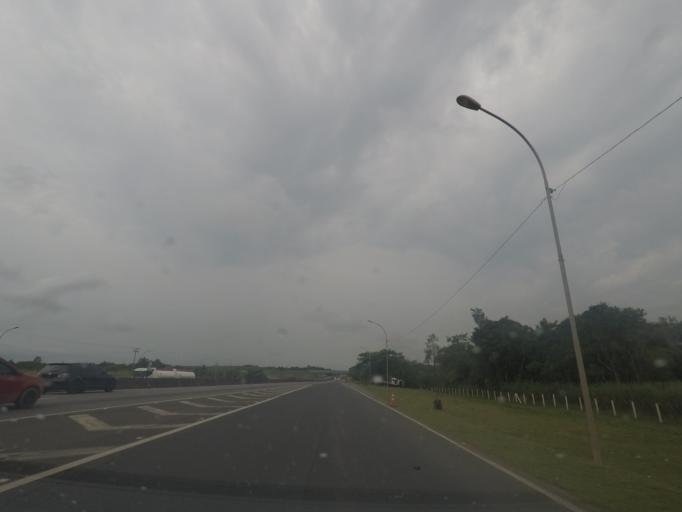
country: BR
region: Sao Paulo
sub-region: Registro
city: Registro
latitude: -24.5349
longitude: -47.8586
